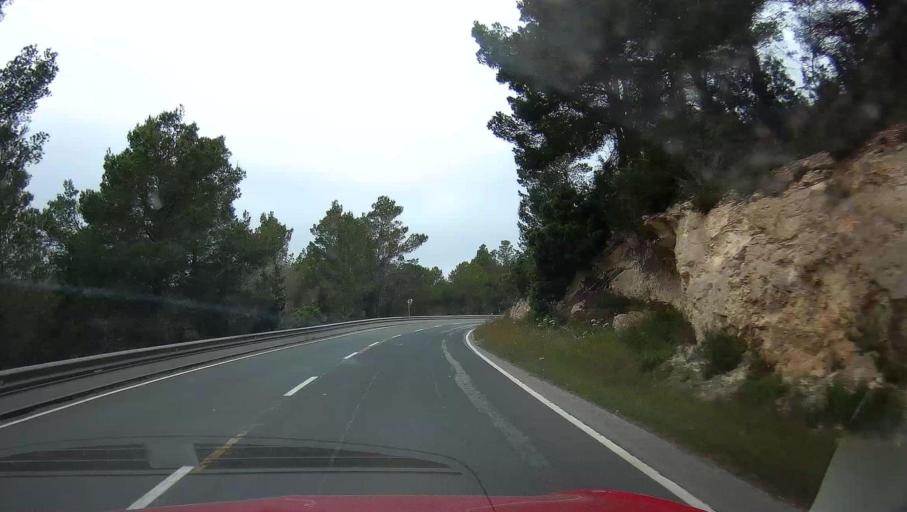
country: ES
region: Balearic Islands
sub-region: Illes Balears
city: Sant Joan de Labritja
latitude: 39.0770
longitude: 1.5029
